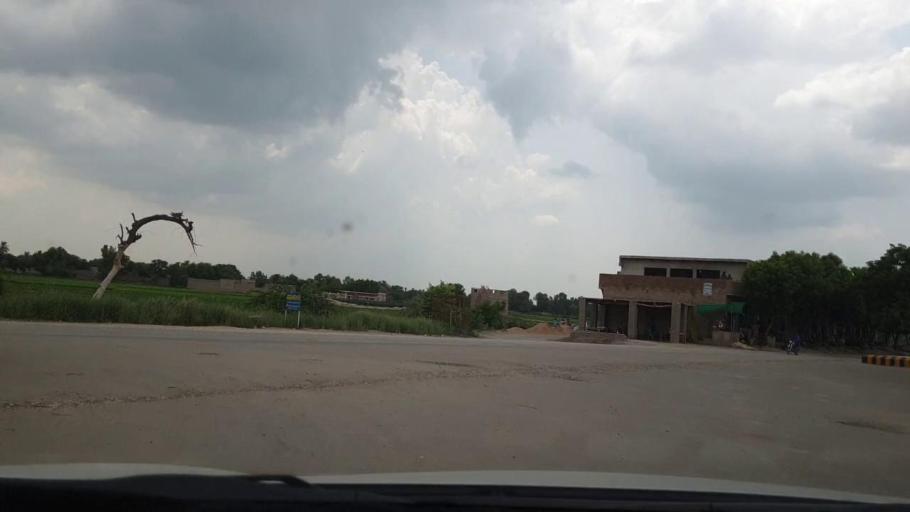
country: PK
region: Sindh
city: Dokri
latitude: 27.3222
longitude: 68.0997
